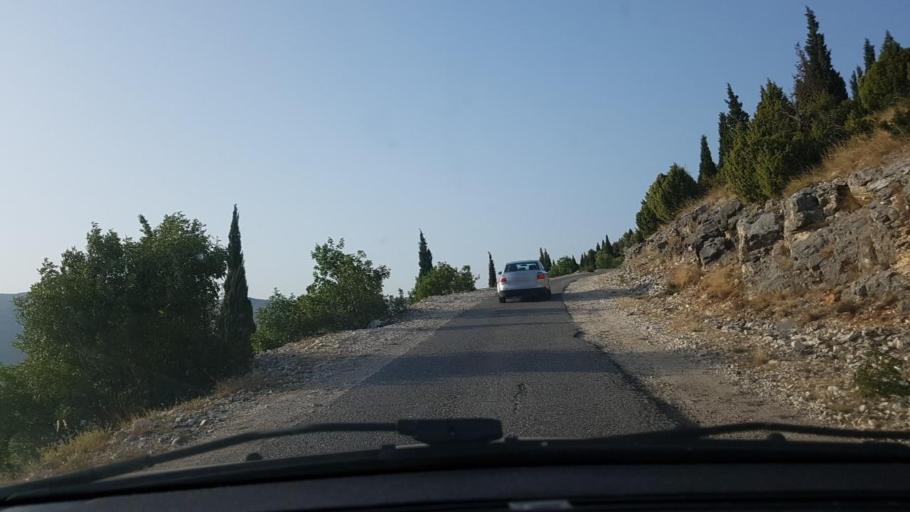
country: BA
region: Federation of Bosnia and Herzegovina
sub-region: Hercegovacko-Bosanski Kanton
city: Mostar
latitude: 43.3482
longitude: 17.8260
